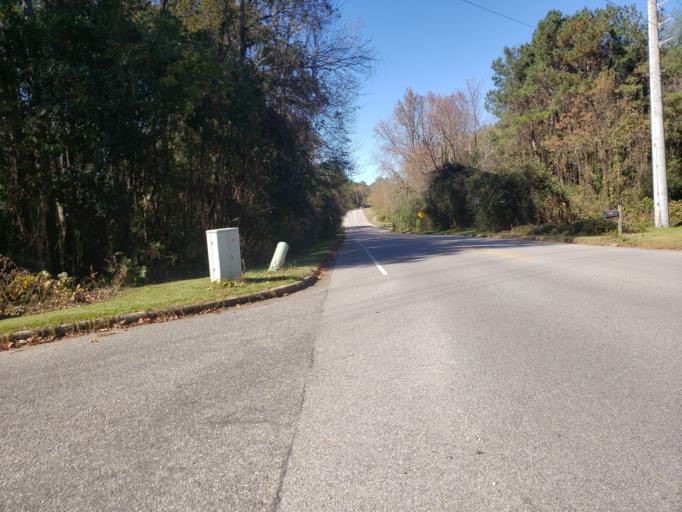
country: US
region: Alabama
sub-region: Lee County
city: Auburn
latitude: 32.5836
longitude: -85.4730
